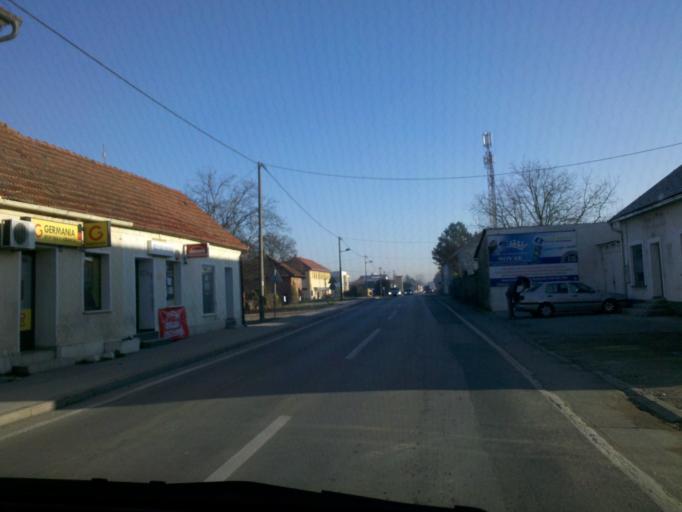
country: HR
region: Medimurska
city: Mala Subotica
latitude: 46.3747
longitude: 16.5265
